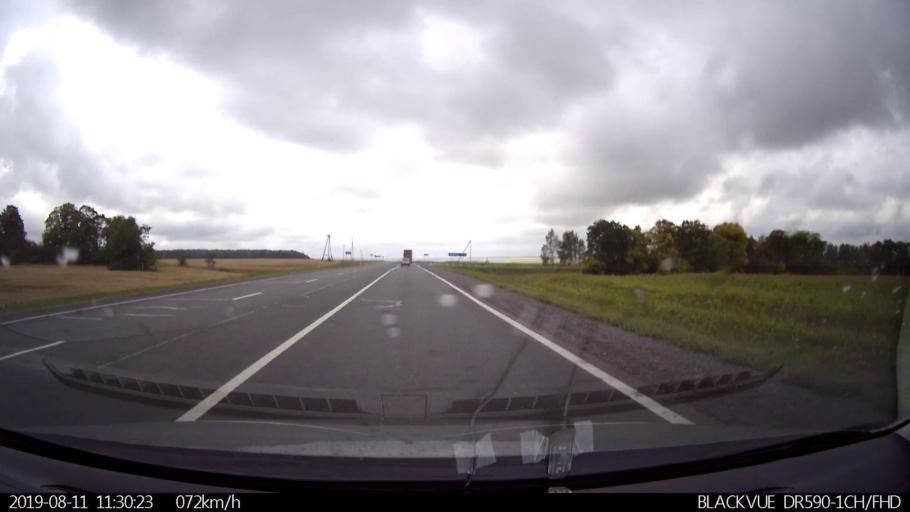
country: RU
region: Ulyanovsk
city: Krasnyy Gulyay
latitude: 54.0592
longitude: 48.2195
